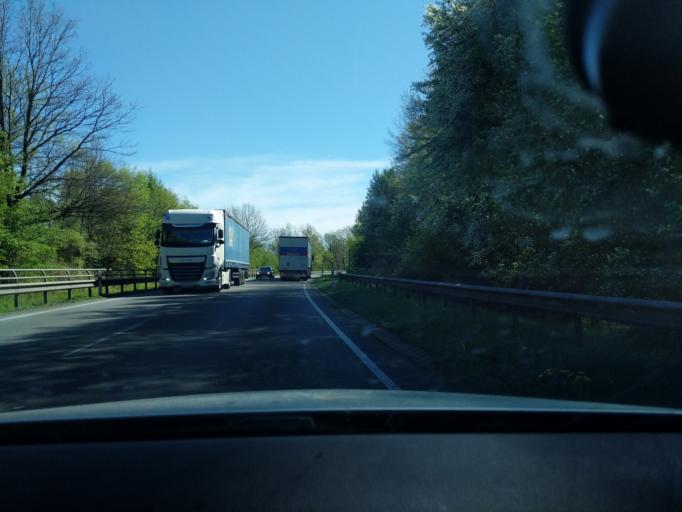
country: DE
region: Lower Saxony
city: Buxtehude
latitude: 53.4612
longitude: 9.7085
